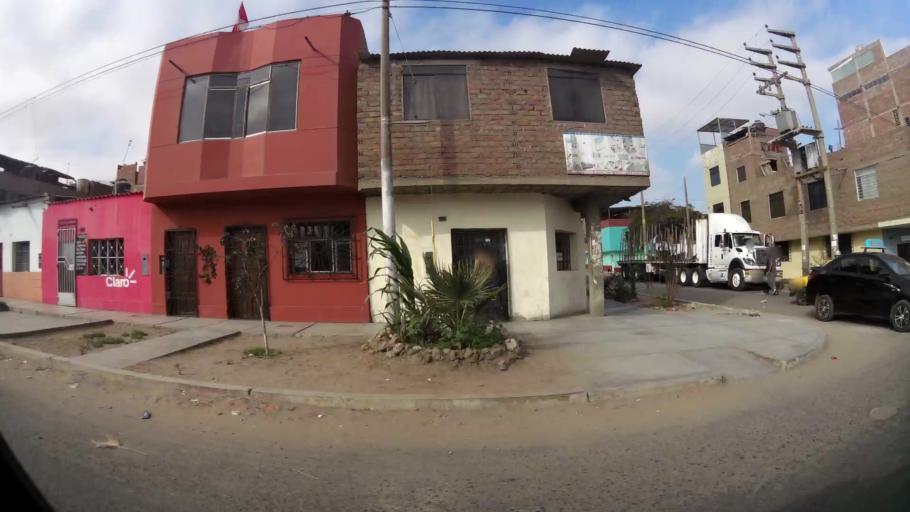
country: PE
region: La Libertad
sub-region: Provincia de Trujillo
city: La Esperanza
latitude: -8.0811
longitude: -79.0439
